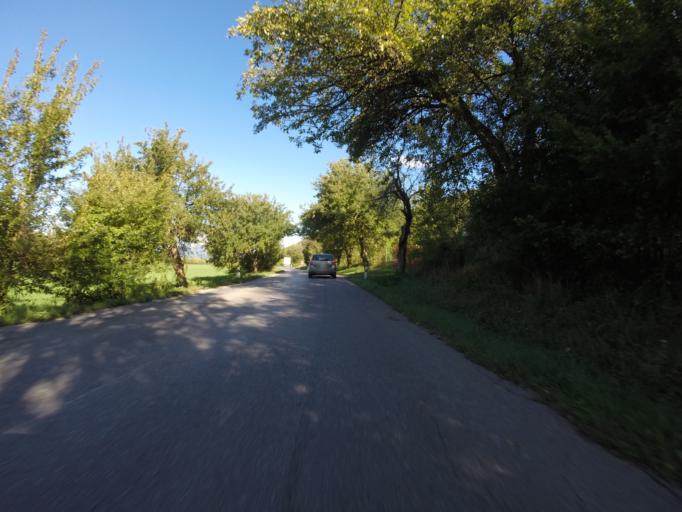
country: SK
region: Nitriansky
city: Ilava
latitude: 48.9909
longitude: 18.2725
